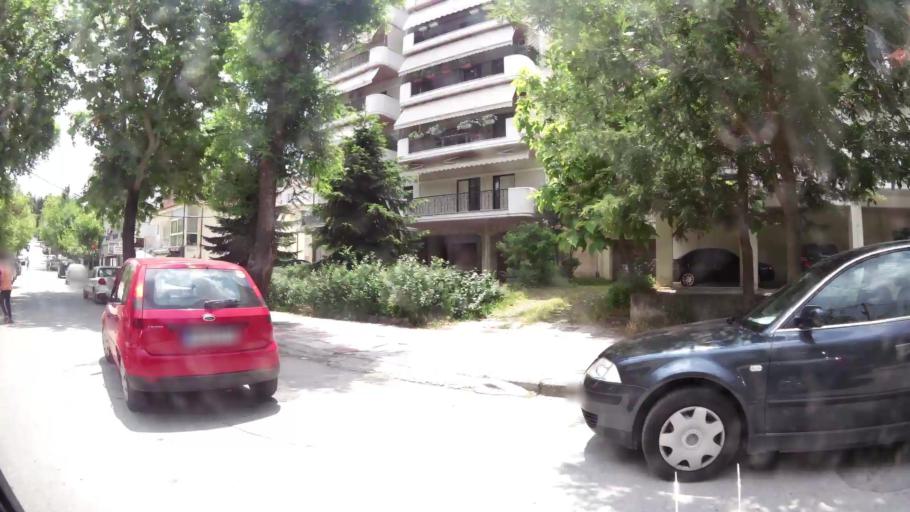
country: GR
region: West Macedonia
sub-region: Nomos Kozanis
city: Kozani
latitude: 40.2937
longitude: 21.7859
